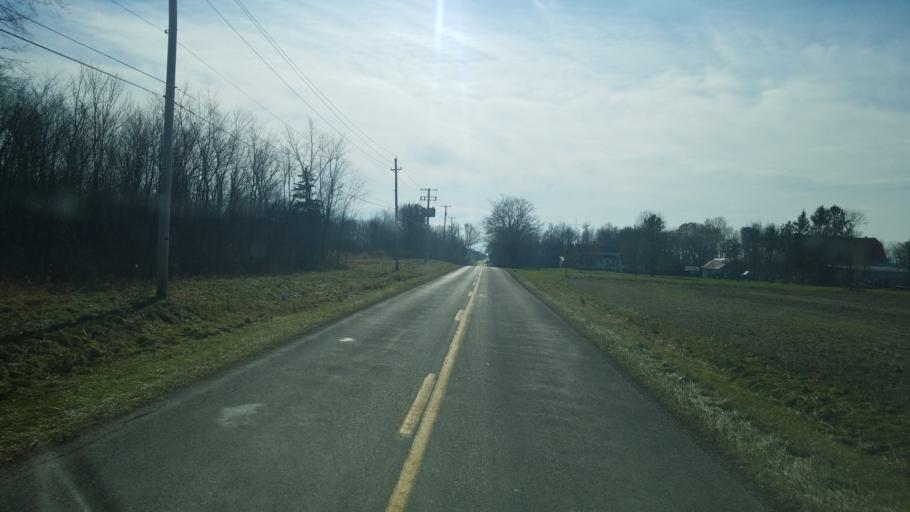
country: US
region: Ohio
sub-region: Ashtabula County
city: Roaming Shores
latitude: 41.6948
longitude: -80.8359
